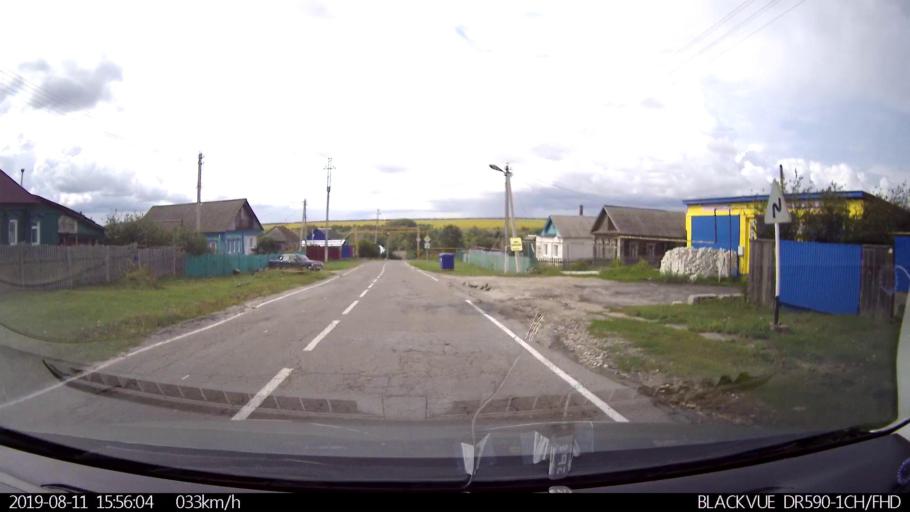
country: RU
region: Ulyanovsk
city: Ignatovka
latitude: 53.9474
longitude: 47.6507
